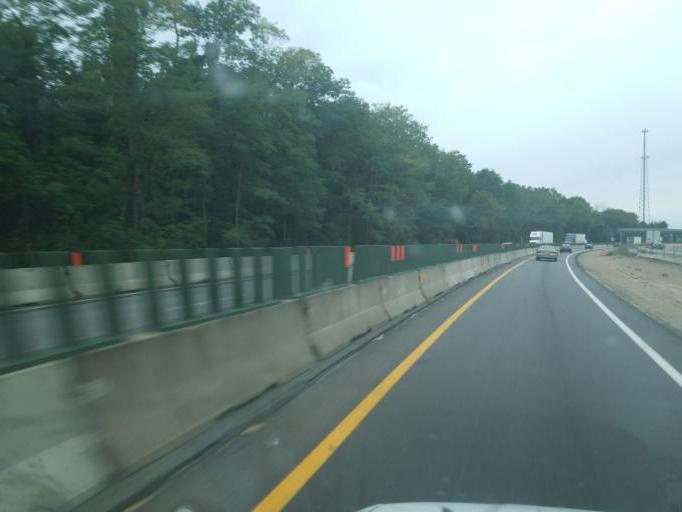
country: US
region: Ohio
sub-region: Summit County
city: Norton
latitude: 41.0404
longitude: -81.6843
